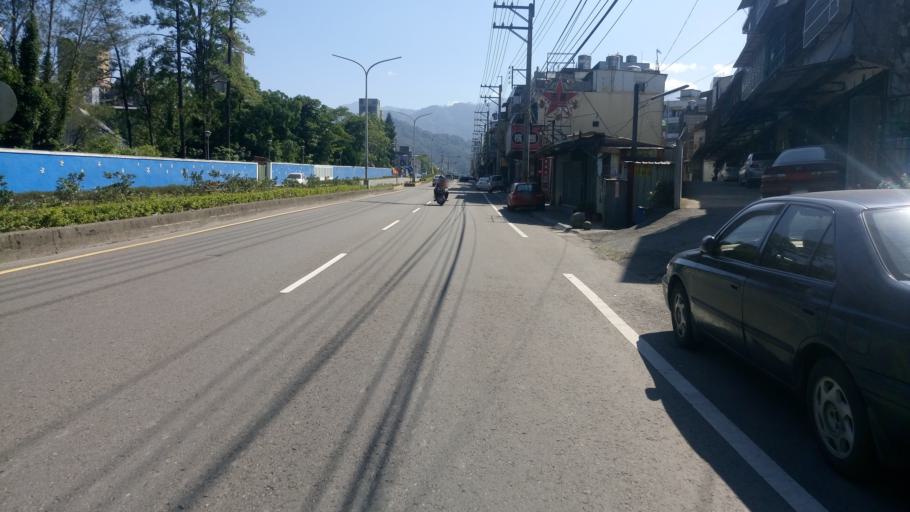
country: TW
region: Taiwan
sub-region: Hsinchu
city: Zhubei
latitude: 24.7237
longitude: 121.1340
